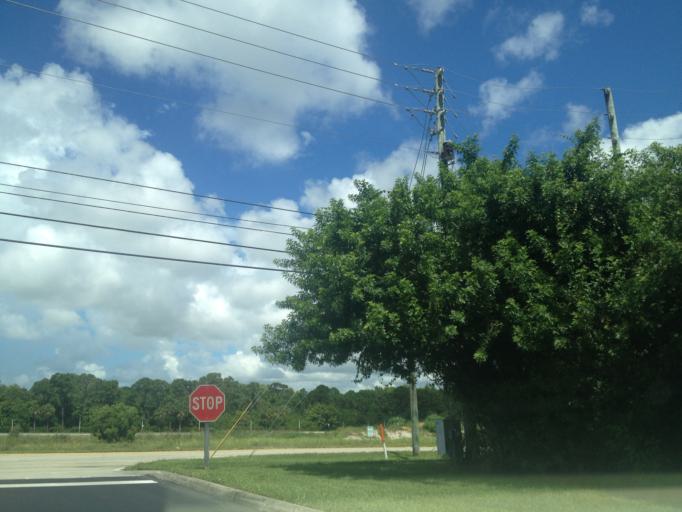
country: US
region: Florida
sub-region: Palm Beach County
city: Hypoluxo
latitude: 26.5599
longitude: -80.0748
